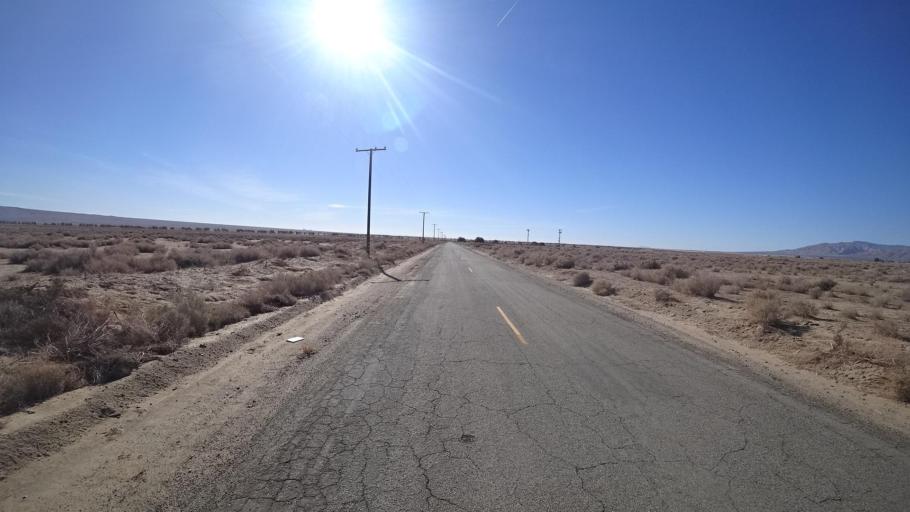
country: US
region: California
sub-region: Kern County
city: California City
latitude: 35.2951
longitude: -117.9681
